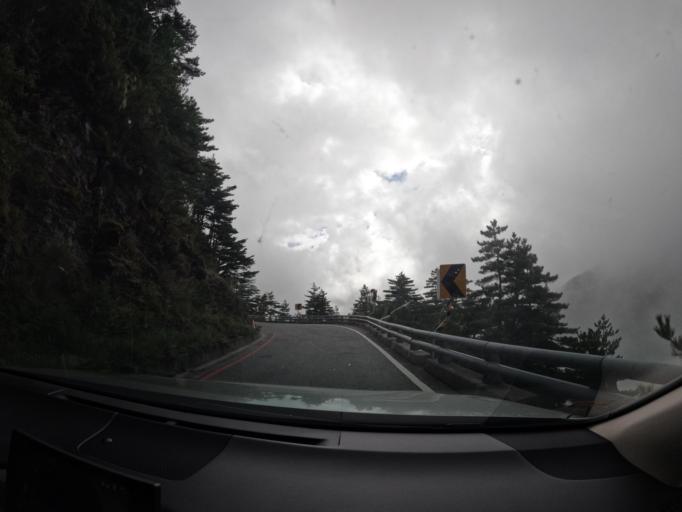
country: TW
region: Taiwan
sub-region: Taitung
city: Taitung
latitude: 23.2633
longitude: 120.9757
